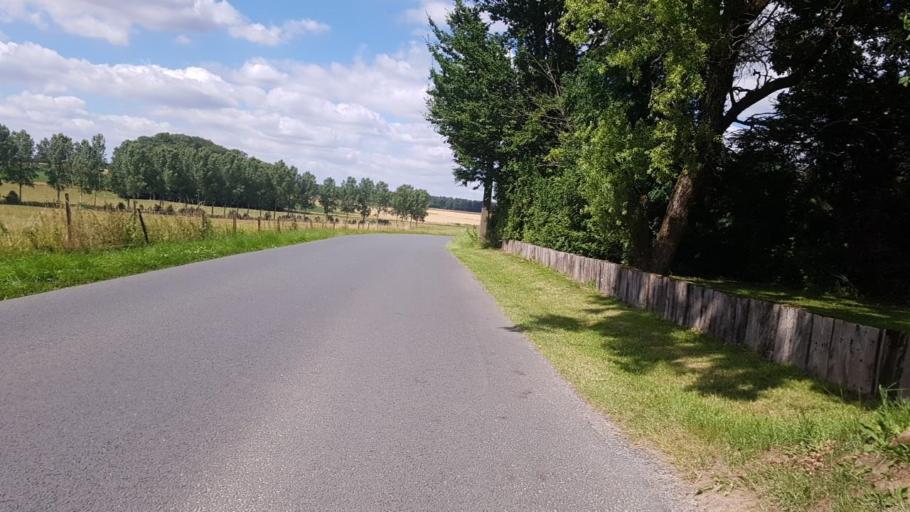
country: BE
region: Wallonia
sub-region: Province de Namur
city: Walcourt
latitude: 50.3280
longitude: 4.3808
